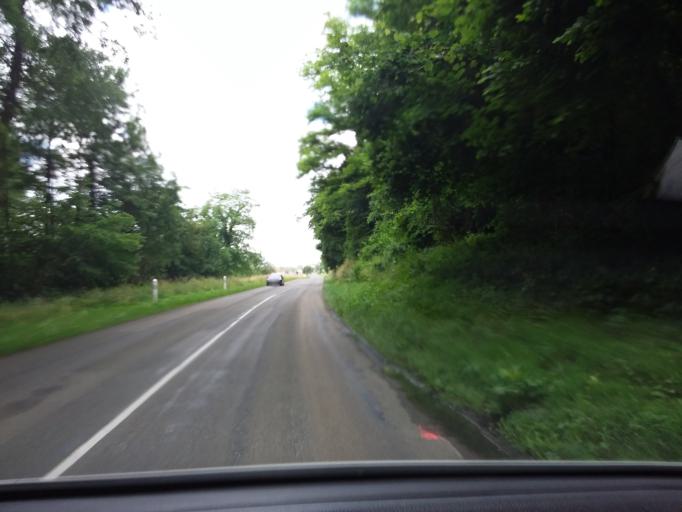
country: FR
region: Picardie
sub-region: Departement de l'Aisne
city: Vailly-sur-Aisne
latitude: 49.4075
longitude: 3.4912
